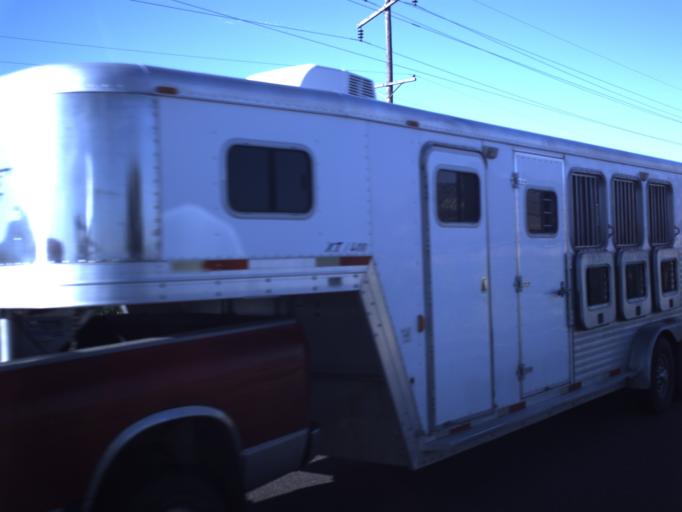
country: US
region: Utah
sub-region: Sevier County
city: Aurora
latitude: 38.9267
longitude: -111.9112
